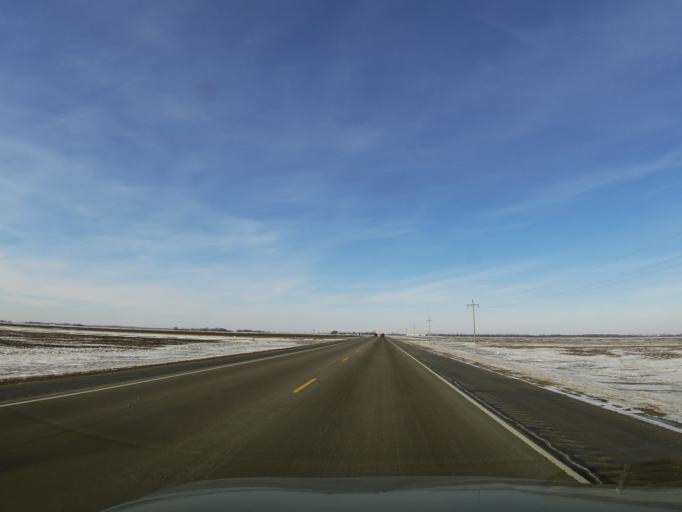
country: US
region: North Dakota
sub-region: Walsh County
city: Grafton
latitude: 48.4124
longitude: -97.3188
